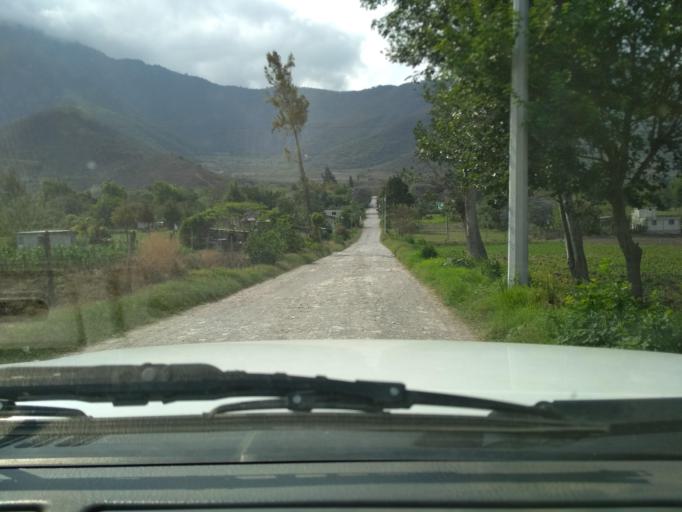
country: MX
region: Veracruz
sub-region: Acultzingo
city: Acatla
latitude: 18.7664
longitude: -97.2273
